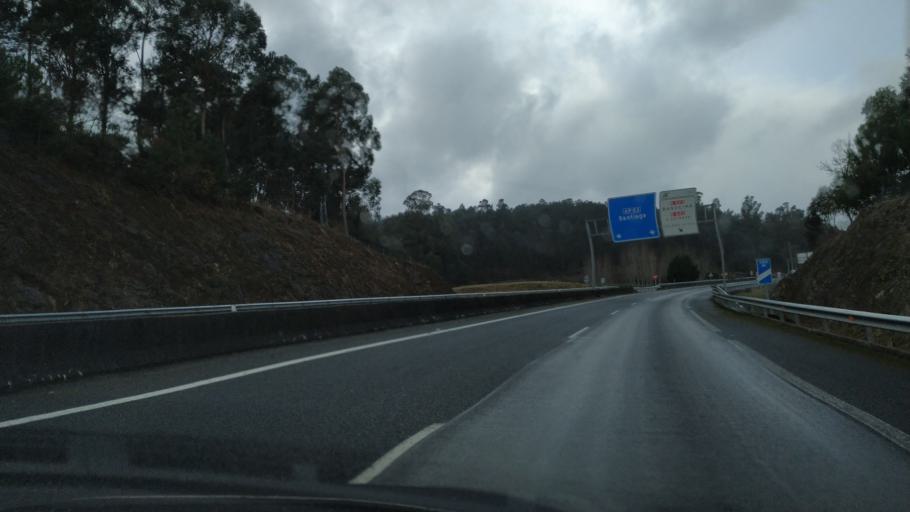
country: ES
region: Galicia
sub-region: Provincia de Pontevedra
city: Silleda
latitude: 42.7291
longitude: -8.3353
